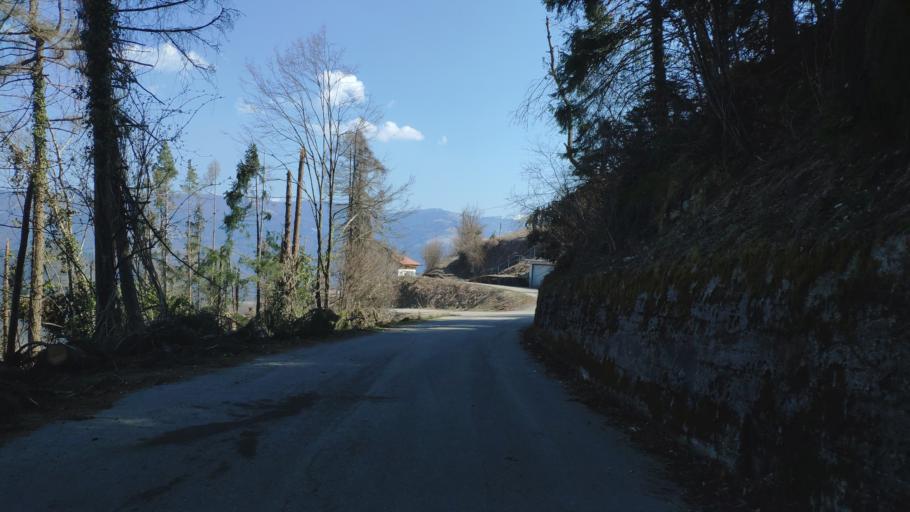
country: IT
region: Veneto
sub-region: Provincia di Vicenza
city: Enego
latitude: 45.9496
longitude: 11.7011
